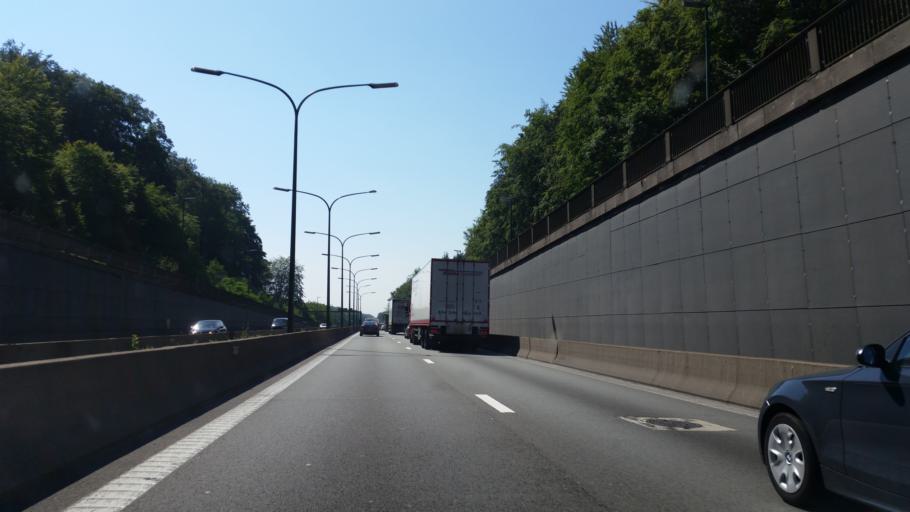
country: BE
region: Flanders
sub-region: Provincie Vlaams-Brabant
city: Wezembeek-Oppem
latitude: 50.8176
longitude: 4.4754
